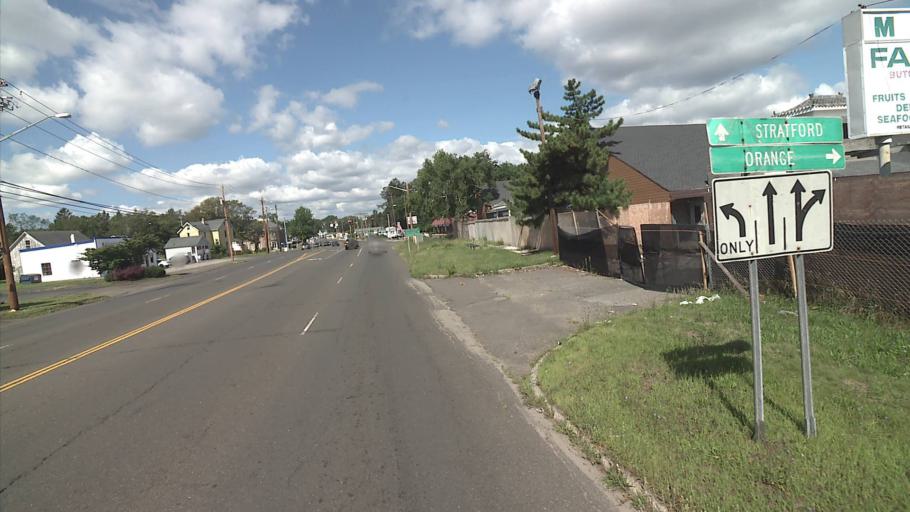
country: US
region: Connecticut
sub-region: New Haven County
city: Milford
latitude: 41.2323
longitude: -73.0544
